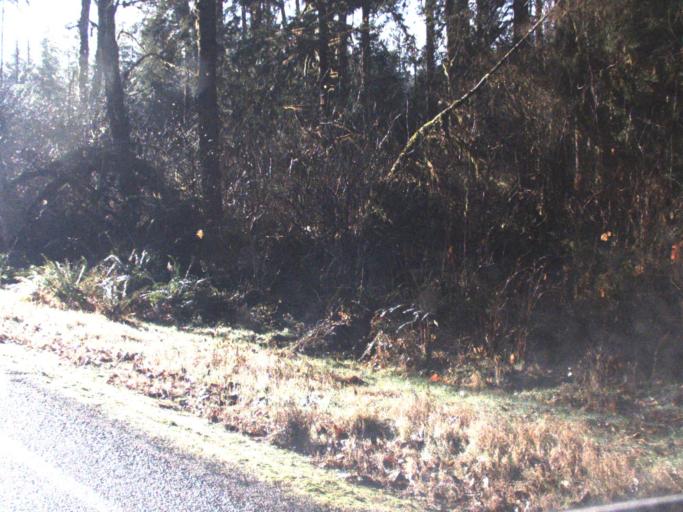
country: US
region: Washington
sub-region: Snohomish County
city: Darrington
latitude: 48.3470
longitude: -121.5400
